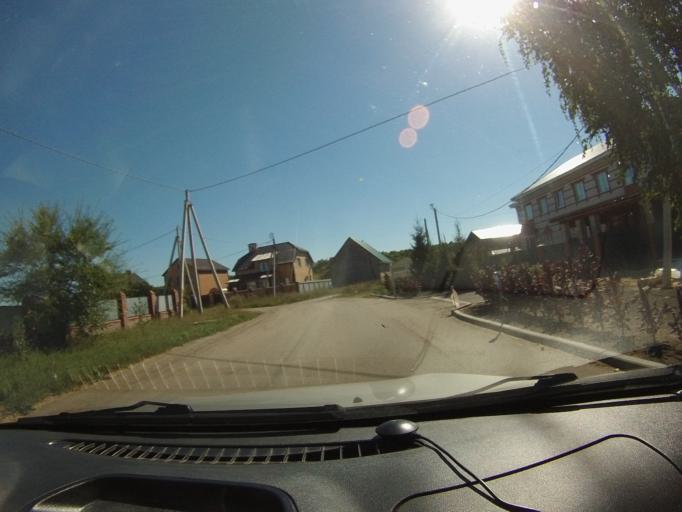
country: RU
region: Tambov
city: Komsomolets
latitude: 52.7617
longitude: 41.3625
